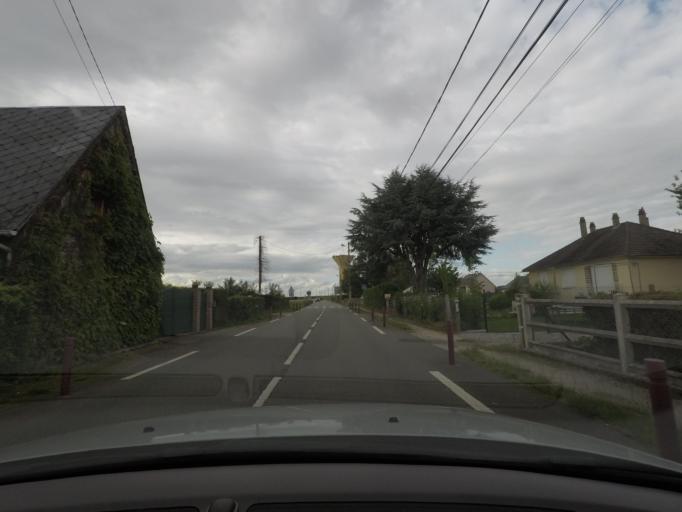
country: FR
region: Haute-Normandie
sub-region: Departement de la Seine-Maritime
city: Ymare
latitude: 49.3535
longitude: 1.1832
